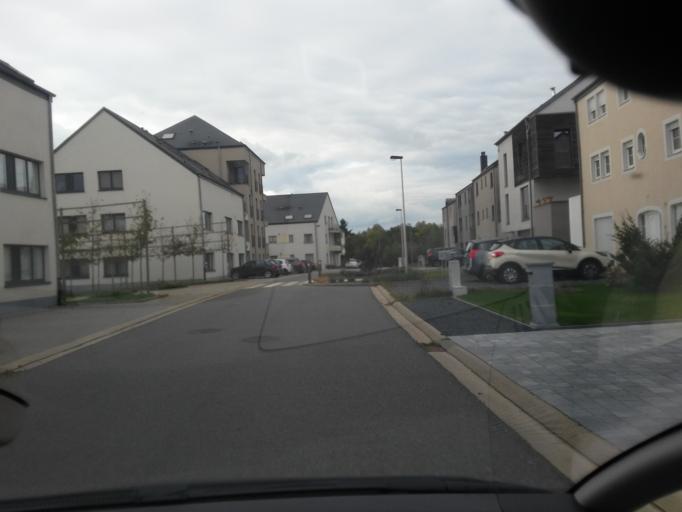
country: BE
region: Wallonia
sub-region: Province du Luxembourg
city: Arlon
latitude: 49.6941
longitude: 5.8077
